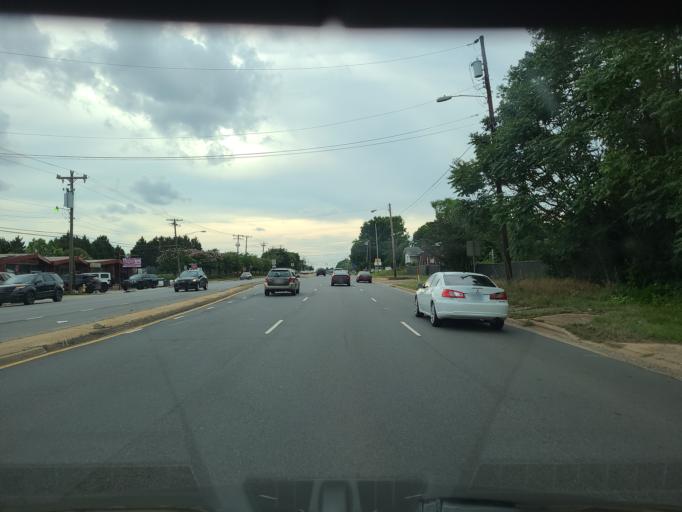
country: US
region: North Carolina
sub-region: Mecklenburg County
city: Charlotte
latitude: 35.2334
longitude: -80.9294
